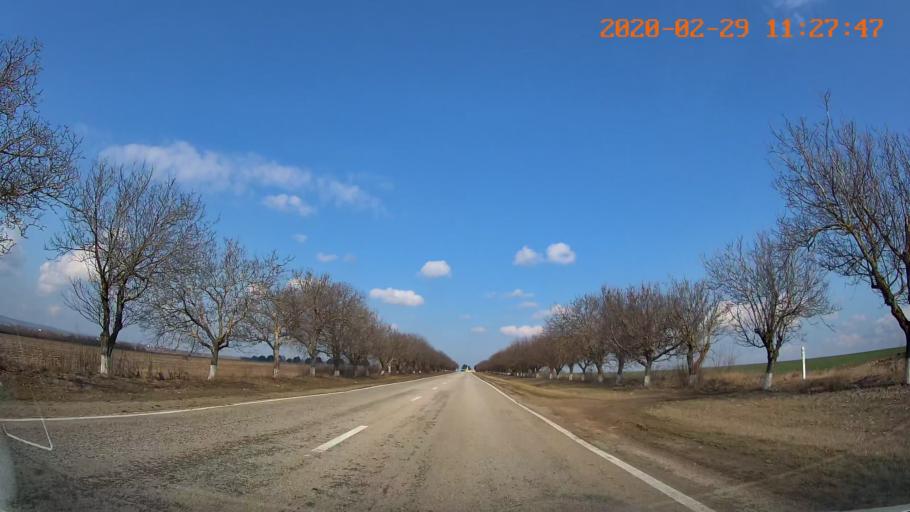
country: MD
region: Telenesti
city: Cocieri
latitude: 47.4737
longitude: 29.1410
